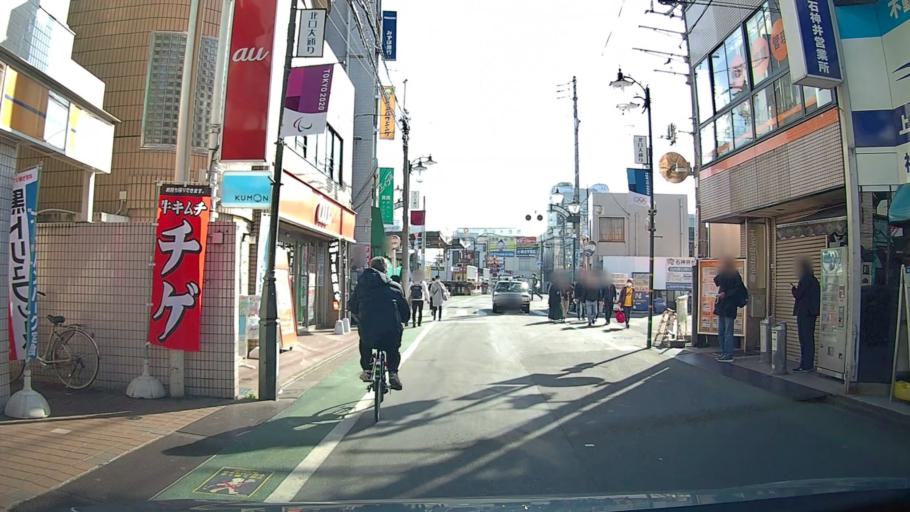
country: JP
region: Tokyo
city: Musashino
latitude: 35.7269
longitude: 139.5914
